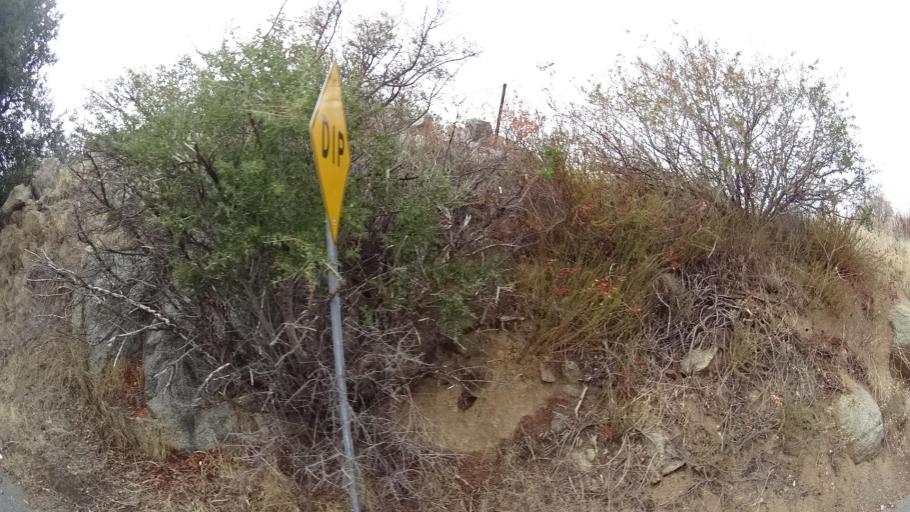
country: US
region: California
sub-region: San Diego County
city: Descanso
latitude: 32.9027
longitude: -116.6440
